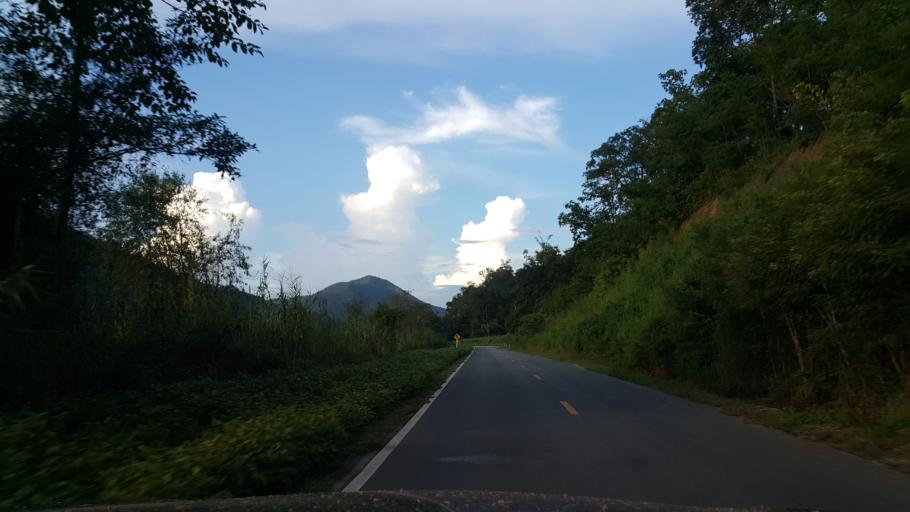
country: TH
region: Mae Hong Son
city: Mae Hi
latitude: 19.2269
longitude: 98.4416
